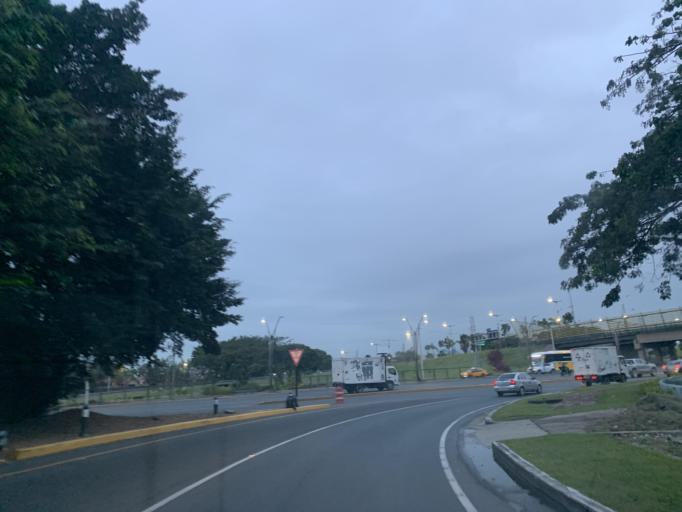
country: EC
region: Guayas
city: Eloy Alfaro
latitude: -2.1530
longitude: -79.8665
